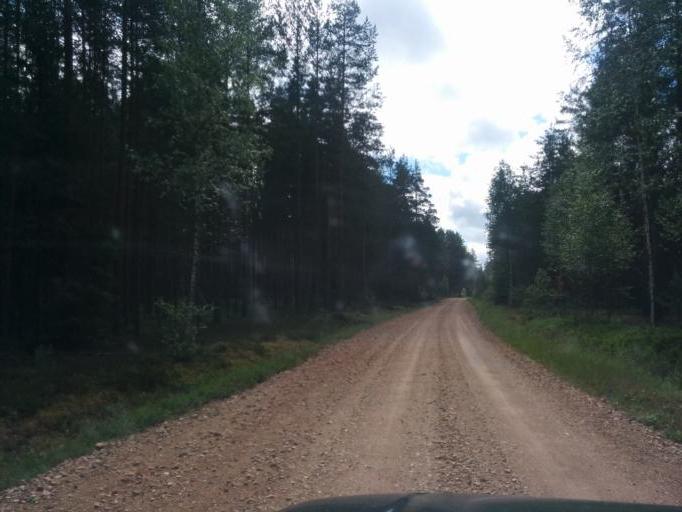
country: LV
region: Vilaka
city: Vilaka
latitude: 57.3607
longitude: 27.6777
